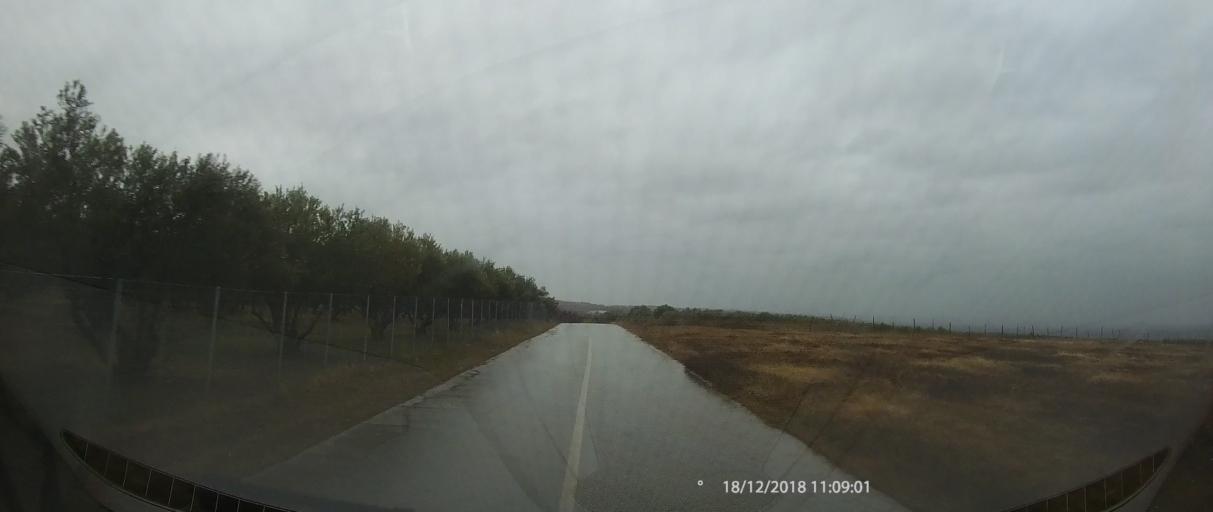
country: GR
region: Central Macedonia
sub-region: Nomos Pierias
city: Lofos
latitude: 40.2300
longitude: 22.3595
